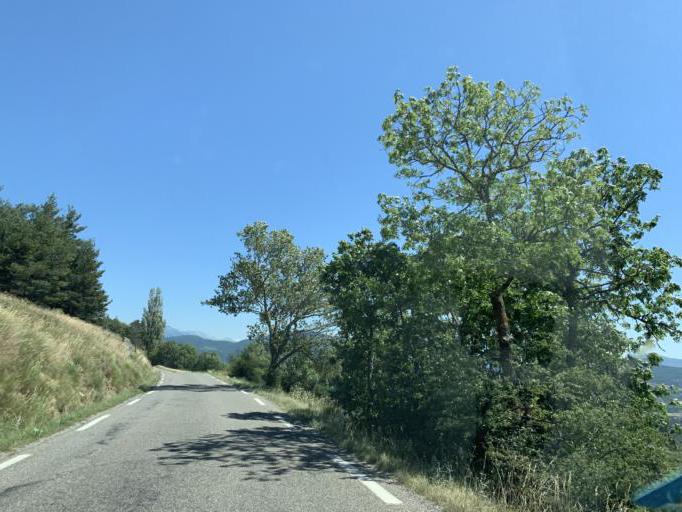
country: FR
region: Provence-Alpes-Cote d'Azur
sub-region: Departement des Hautes-Alpes
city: La Batie-Neuve
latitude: 44.5990
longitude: 6.1460
